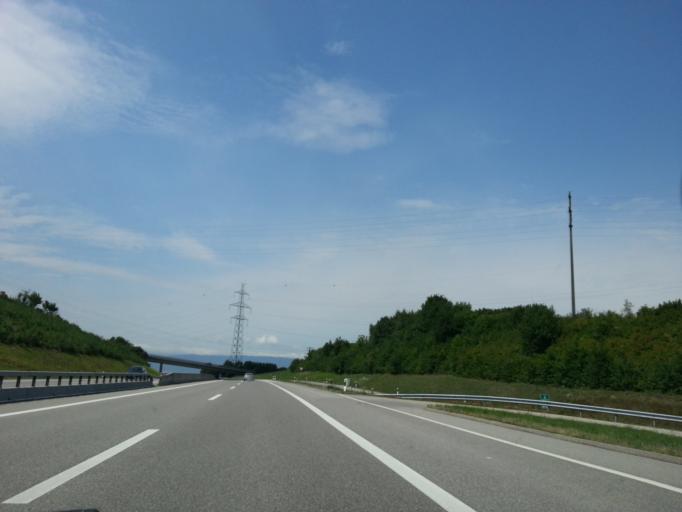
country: CH
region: Fribourg
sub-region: See District
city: Kerzers
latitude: 46.9617
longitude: 7.1913
